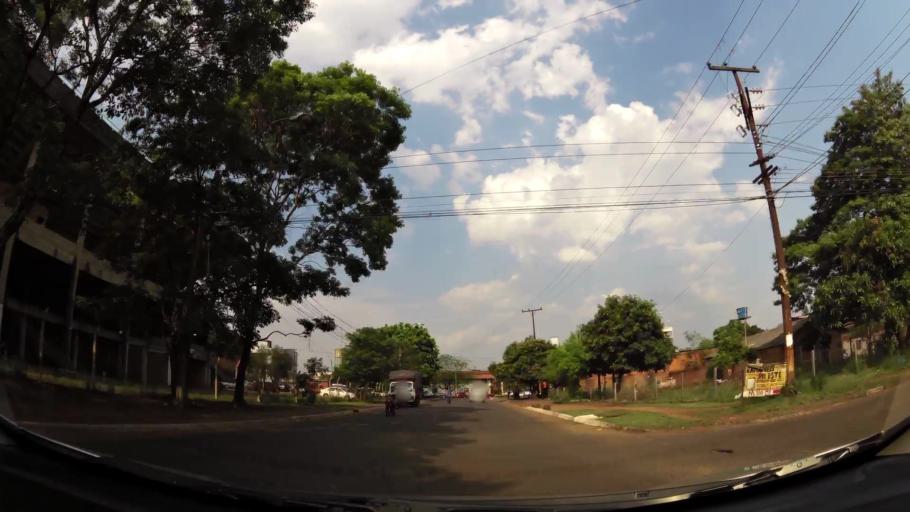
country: PY
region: Alto Parana
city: Presidente Franco
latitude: -25.5281
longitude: -54.6119
